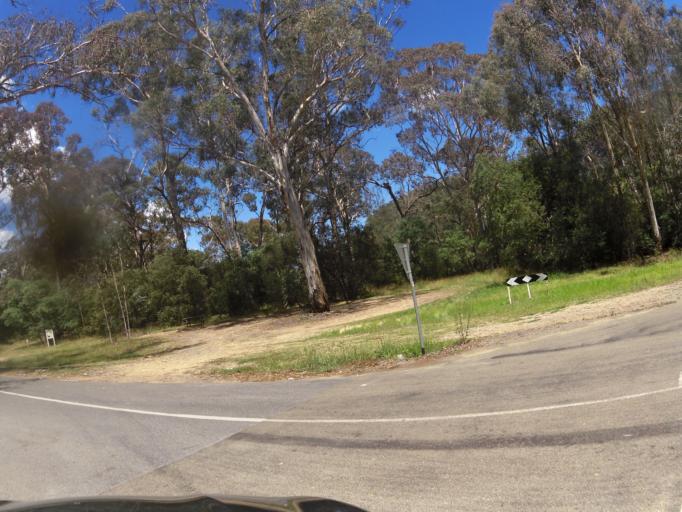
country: AU
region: Victoria
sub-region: Alpine
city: Mount Beauty
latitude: -36.7420
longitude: 147.0148
